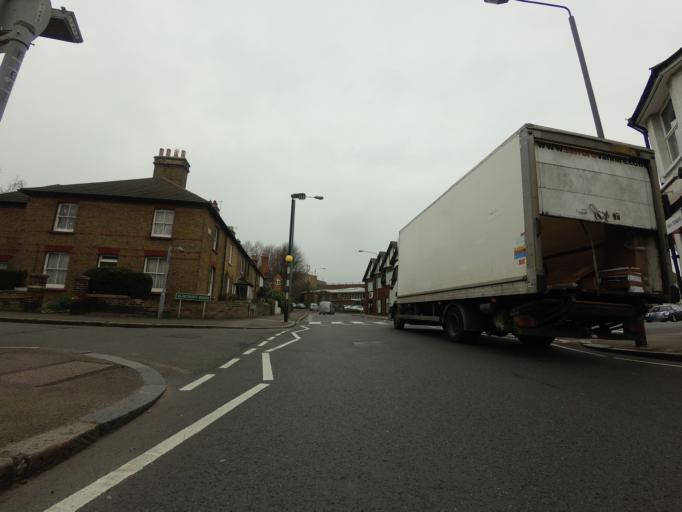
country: GB
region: England
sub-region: Greater London
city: Orpington
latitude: 51.3809
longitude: 0.1025
